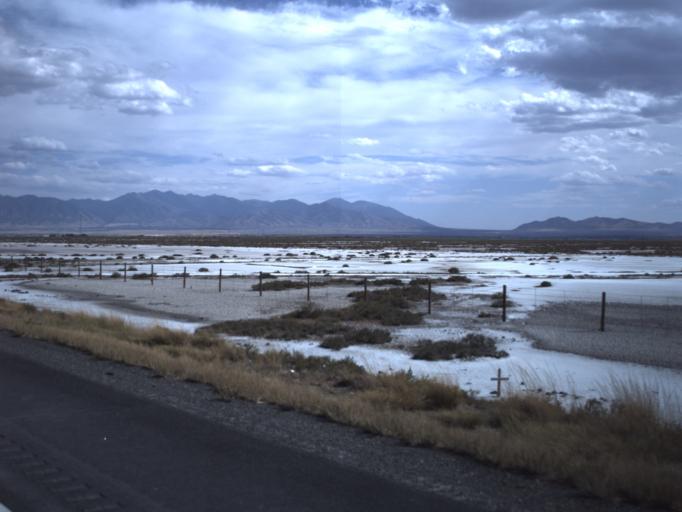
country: US
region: Utah
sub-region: Tooele County
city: Grantsville
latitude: 40.6997
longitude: -112.4868
